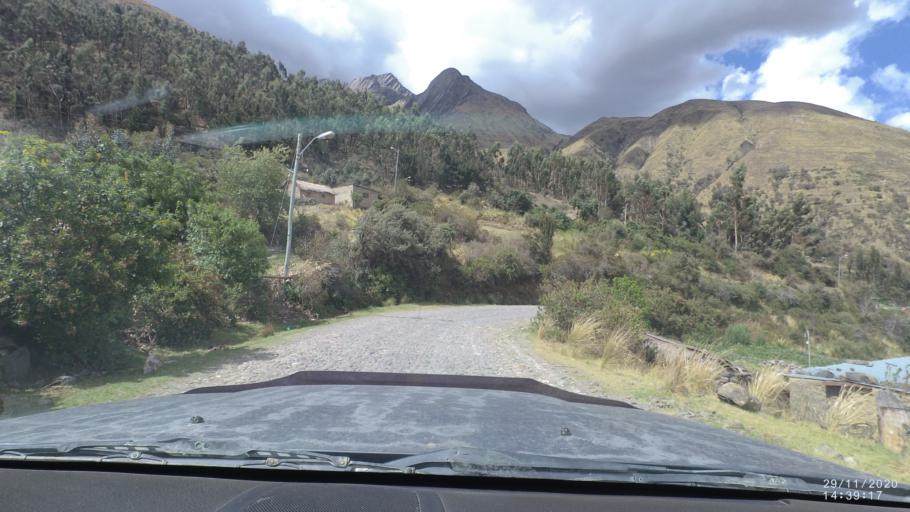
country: BO
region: Cochabamba
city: Sipe Sipe
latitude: -17.2738
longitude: -66.3290
